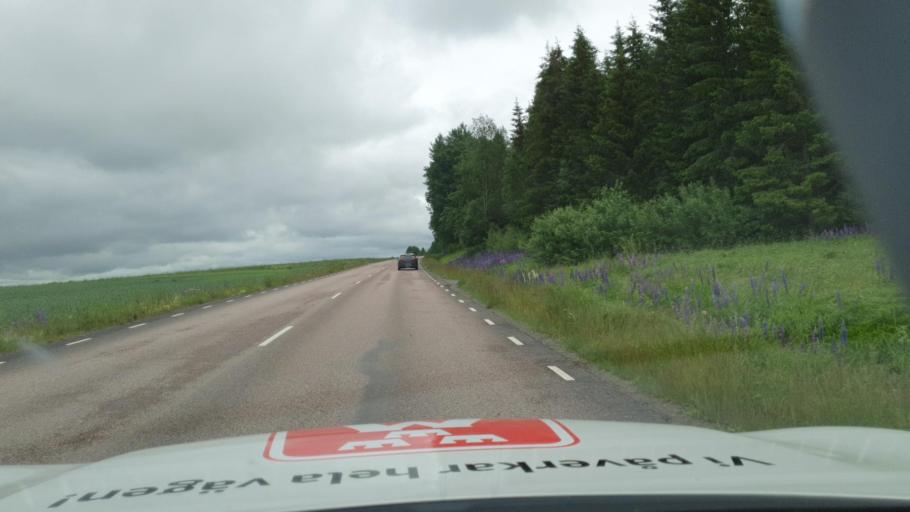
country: SE
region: Vaermland
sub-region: Karlstads Kommun
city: Edsvalla
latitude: 59.4092
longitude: 13.2118
